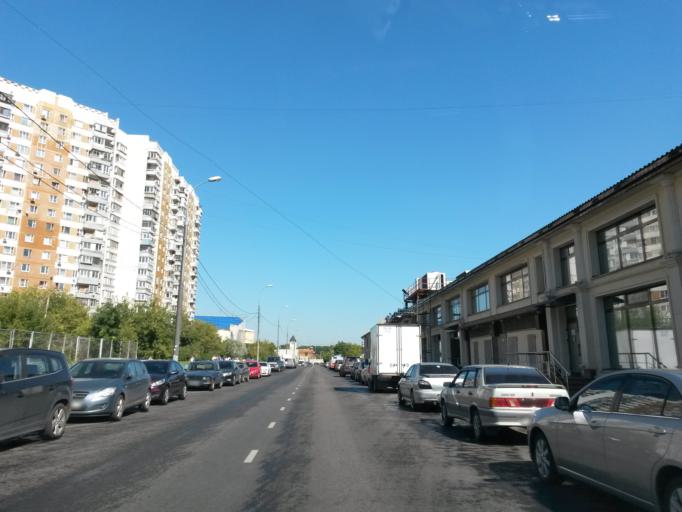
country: RU
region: Moscow
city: Mar'ino
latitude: 55.6521
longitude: 37.7418
